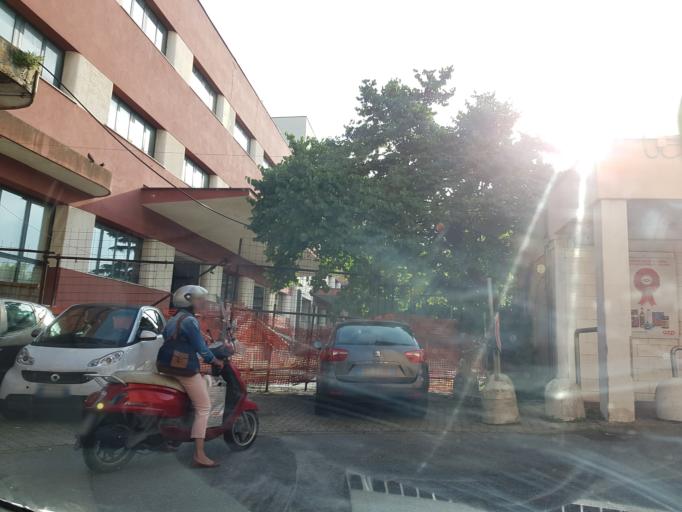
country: IT
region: Liguria
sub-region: Provincia di Genova
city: Genoa
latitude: 44.4042
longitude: 8.9666
